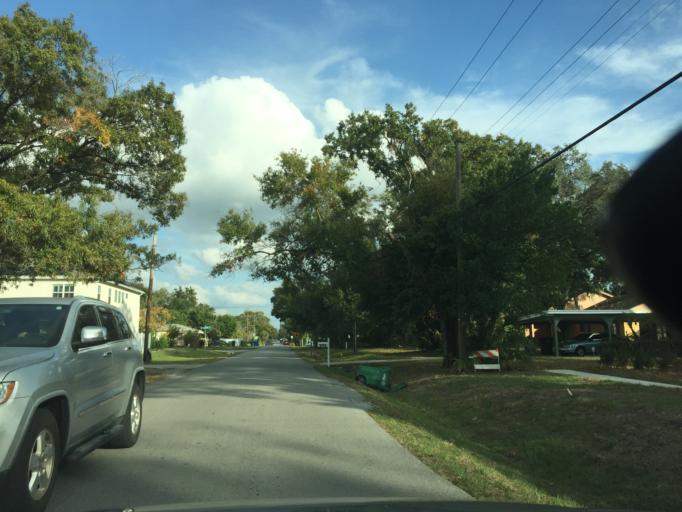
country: US
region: Florida
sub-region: Hillsborough County
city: Tampa
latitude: 27.9459
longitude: -82.4952
